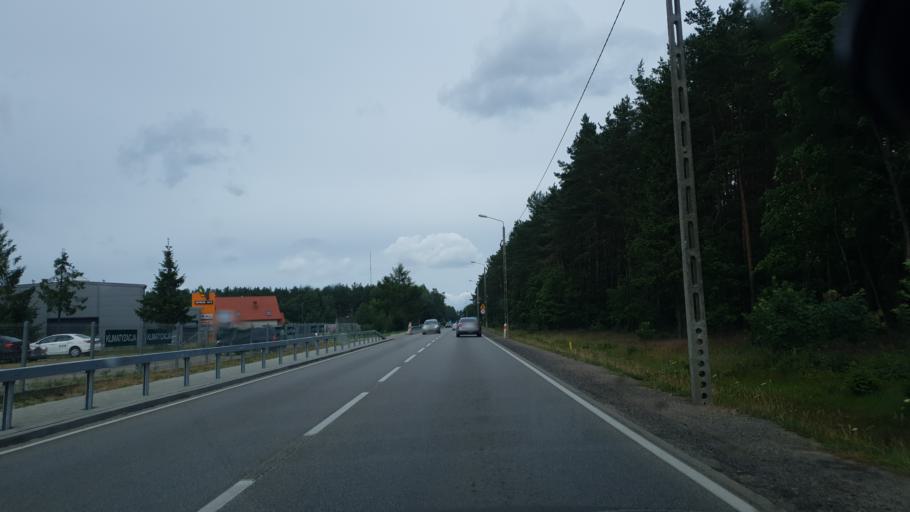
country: PL
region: Pomeranian Voivodeship
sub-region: Powiat kartuski
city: Chwaszczyno
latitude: 54.4338
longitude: 18.3996
